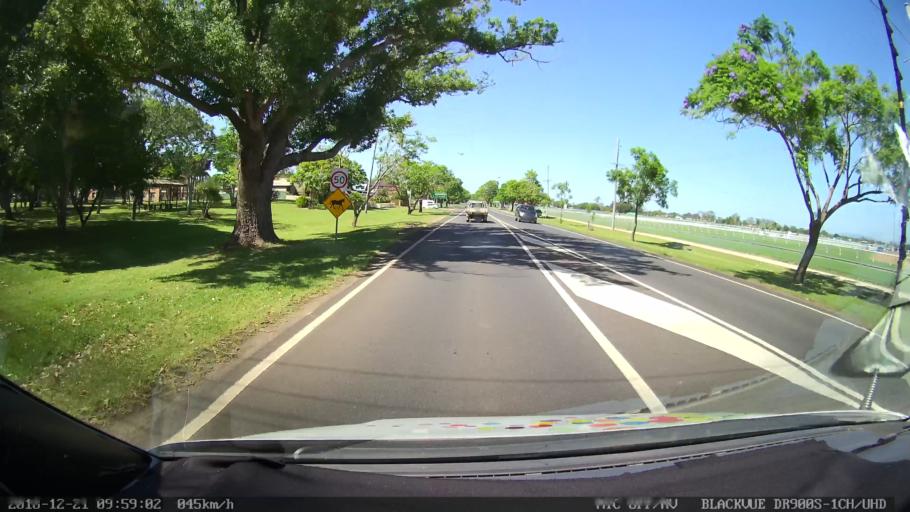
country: AU
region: New South Wales
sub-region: Clarence Valley
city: Grafton
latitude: -29.6758
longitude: 152.9328
